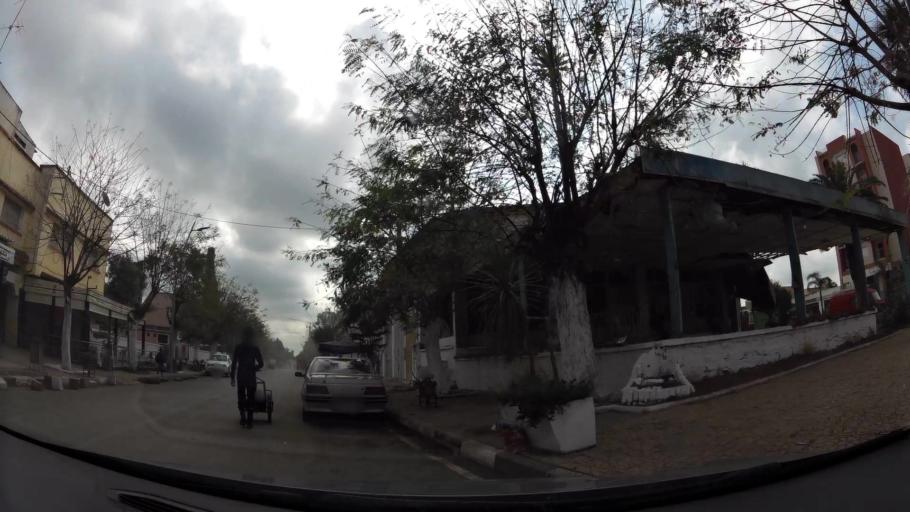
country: MA
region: Rabat-Sale-Zemmour-Zaer
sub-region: Khemisset
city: Tiflet
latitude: 33.8936
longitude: -6.3101
